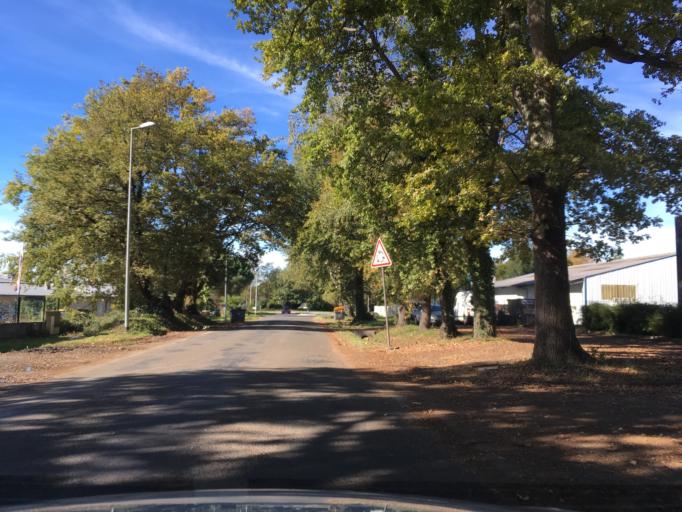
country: FR
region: Aquitaine
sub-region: Departement des Pyrenees-Atlantiques
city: Buros
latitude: 43.3233
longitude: -0.3233
